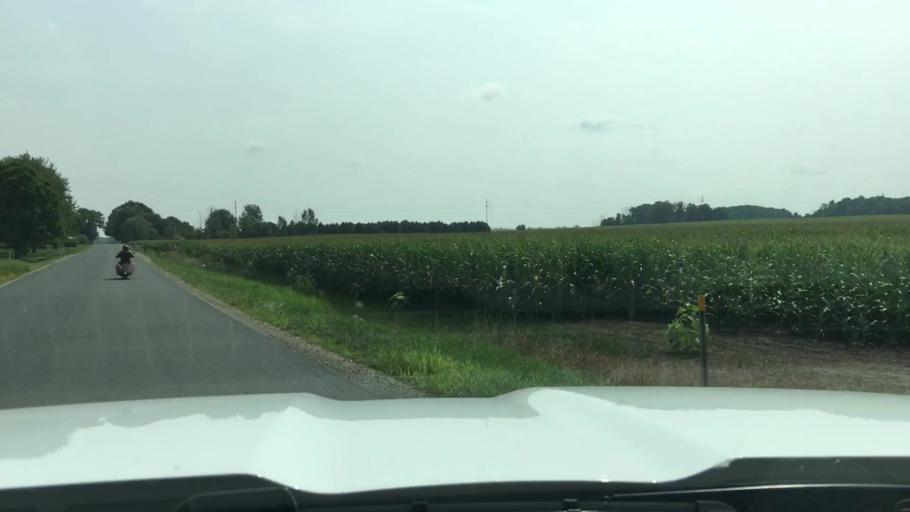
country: US
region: Michigan
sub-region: Eaton County
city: Grand Ledge
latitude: 42.7848
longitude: -84.7588
